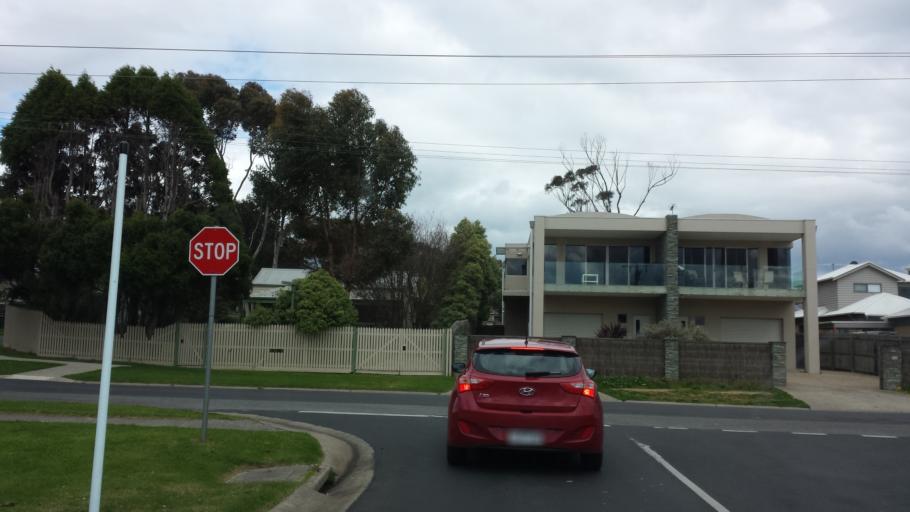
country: AU
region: Victoria
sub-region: Bass Coast
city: Cowes
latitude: -38.4521
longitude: 145.2346
